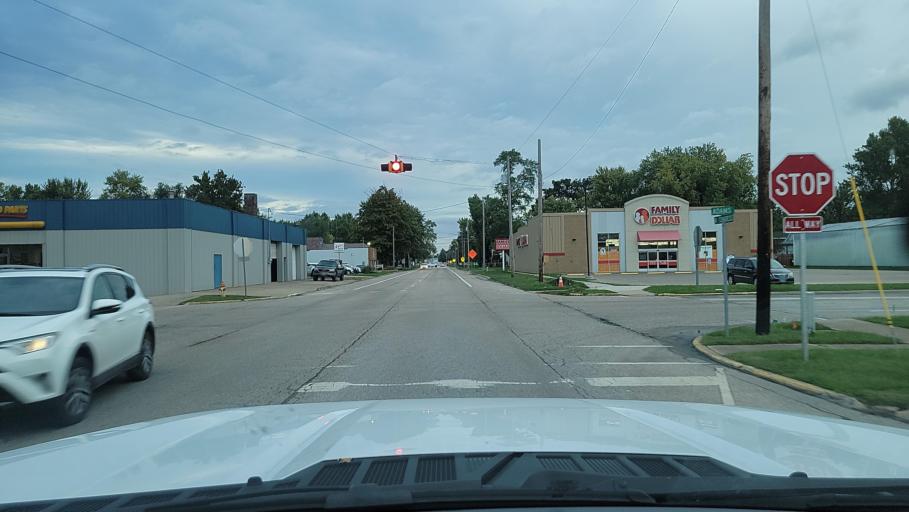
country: US
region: Illinois
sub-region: Schuyler County
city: Rushville
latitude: 40.1236
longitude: -90.5636
